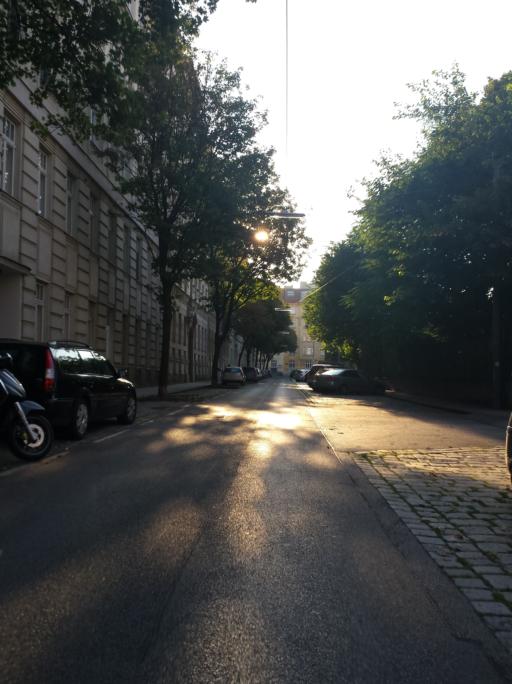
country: AT
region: Vienna
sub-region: Wien Stadt
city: Vienna
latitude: 48.1947
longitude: 16.3912
